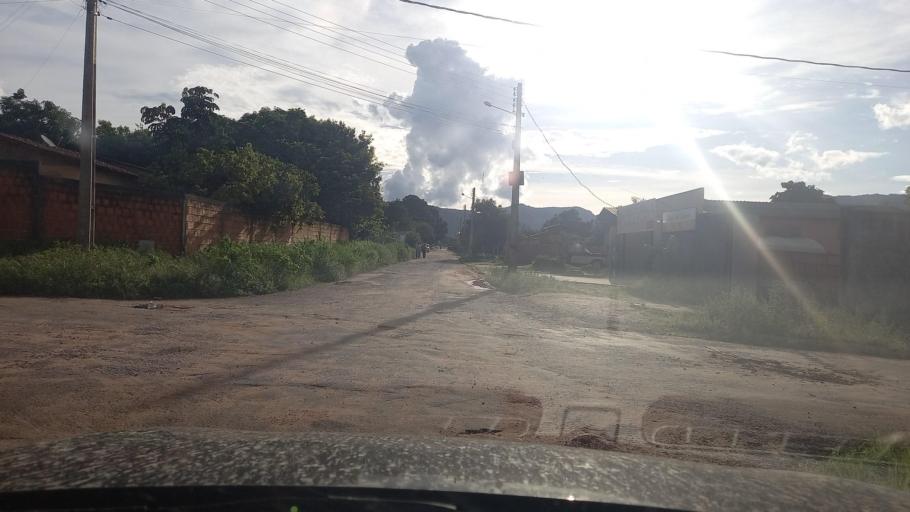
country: BR
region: Goias
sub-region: Cavalcante
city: Cavalcante
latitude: -13.7952
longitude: -47.4444
